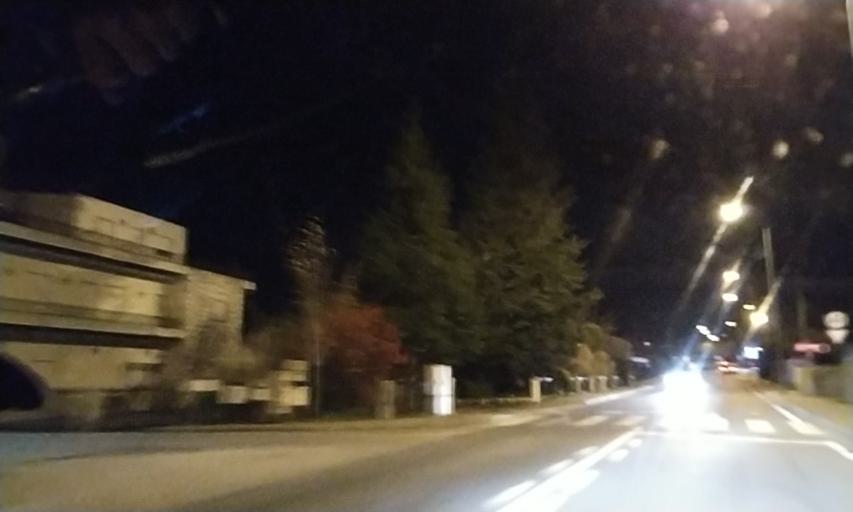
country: PT
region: Castelo Branco
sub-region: Concelho do Fundao
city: Fundao
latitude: 40.1644
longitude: -7.4970
